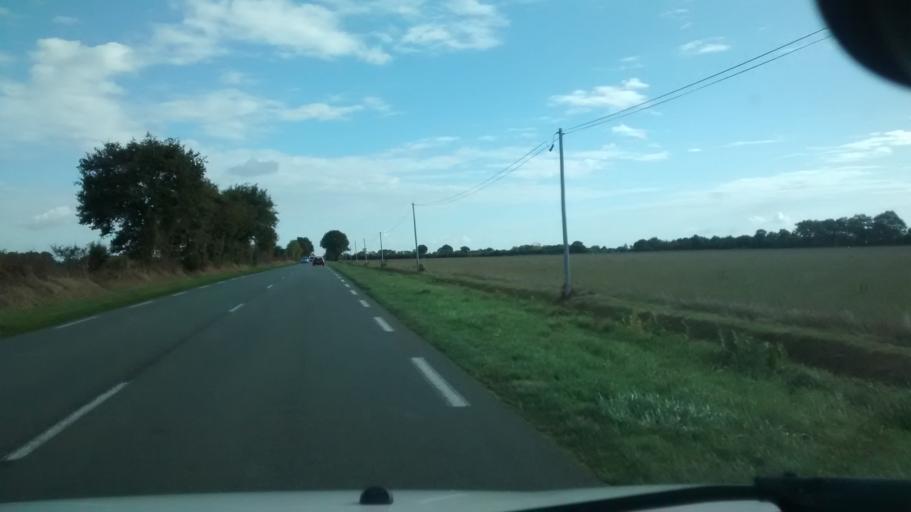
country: FR
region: Pays de la Loire
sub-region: Departement de Maine-et-Loire
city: Pouance
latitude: 47.7443
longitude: -1.2253
